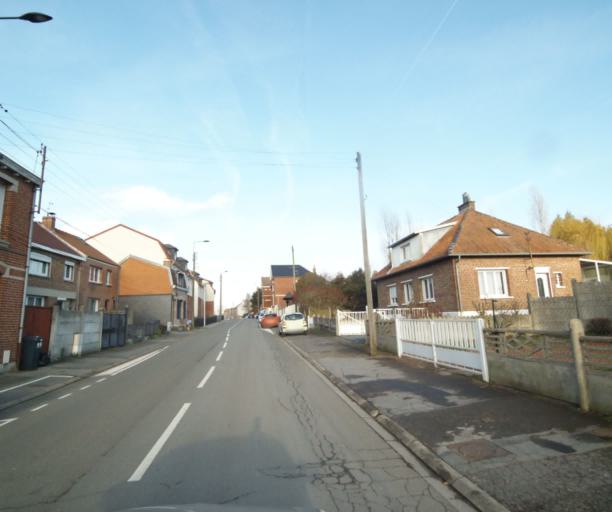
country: FR
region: Nord-Pas-de-Calais
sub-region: Departement du Nord
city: Saint-Saulve
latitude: 50.3639
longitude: 3.5425
